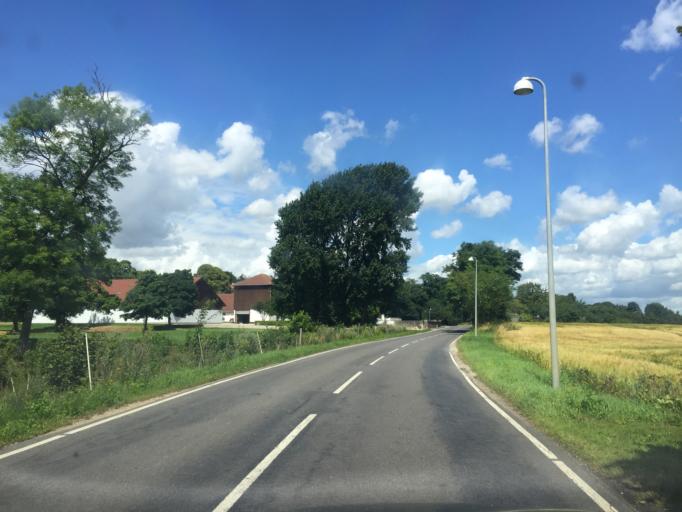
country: DK
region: Capital Region
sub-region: Hoje-Taastrup Kommune
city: Taastrup
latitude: 55.6895
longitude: 12.2456
